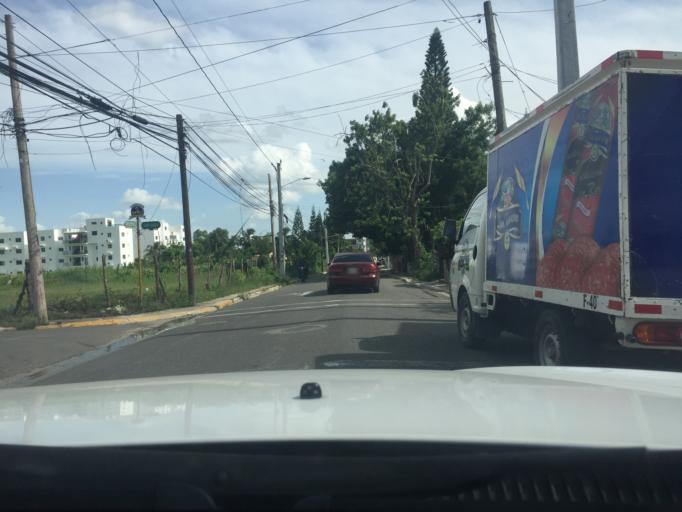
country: DO
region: Santiago
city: Tamboril
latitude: 19.4832
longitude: -70.6551
